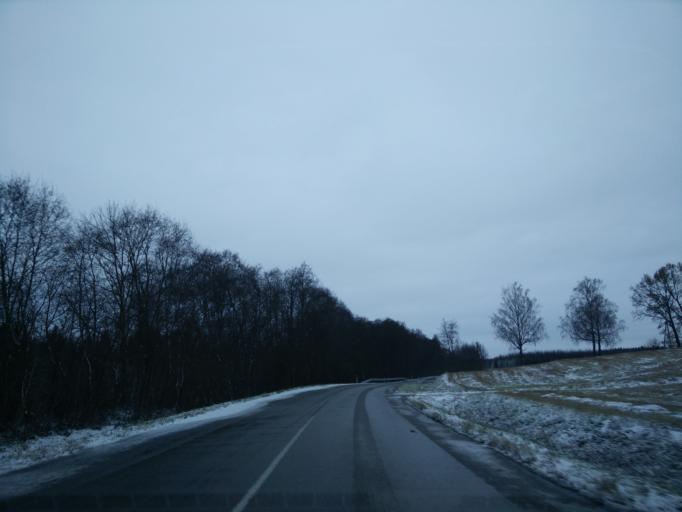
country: LT
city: Tytuveneliai
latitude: 55.5032
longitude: 23.2996
